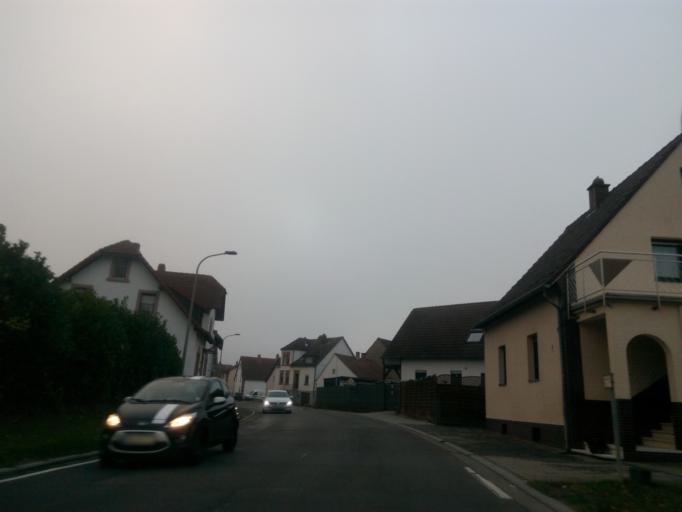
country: DE
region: Rheinland-Pfalz
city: Rothselberg
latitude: 49.5499
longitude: 7.5971
